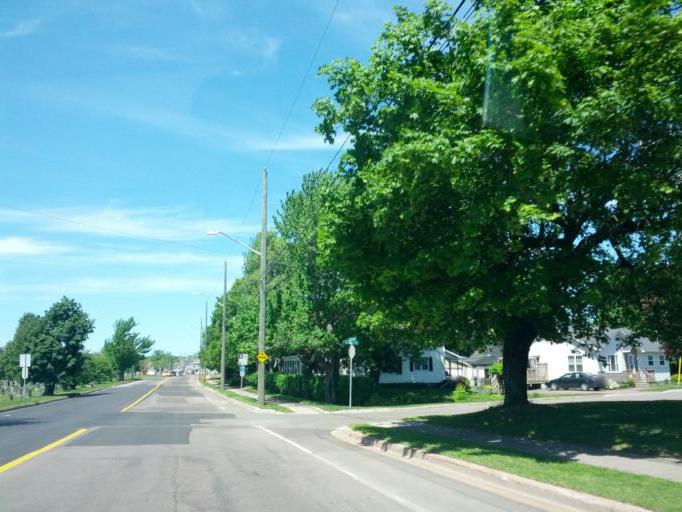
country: CA
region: New Brunswick
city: Moncton
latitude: 46.1096
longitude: -64.7747
